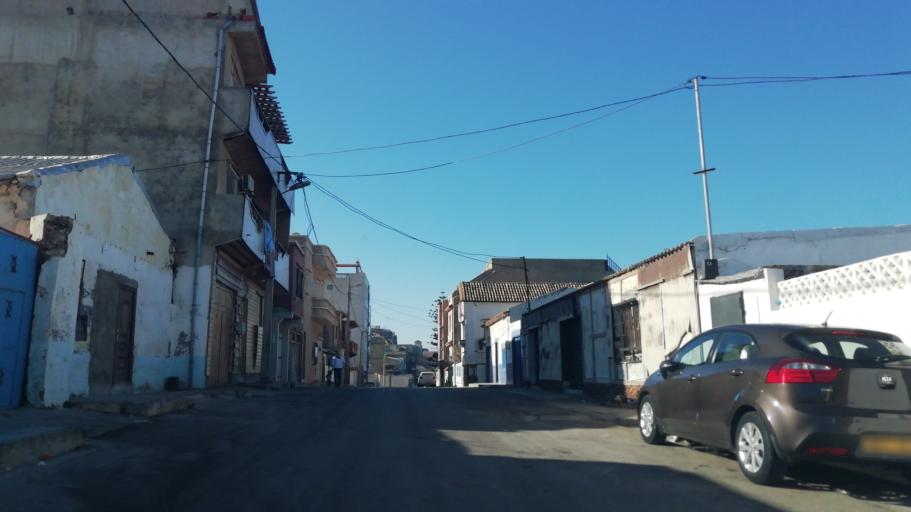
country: DZ
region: Oran
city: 'Ain el Turk
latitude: 35.7294
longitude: -0.8452
